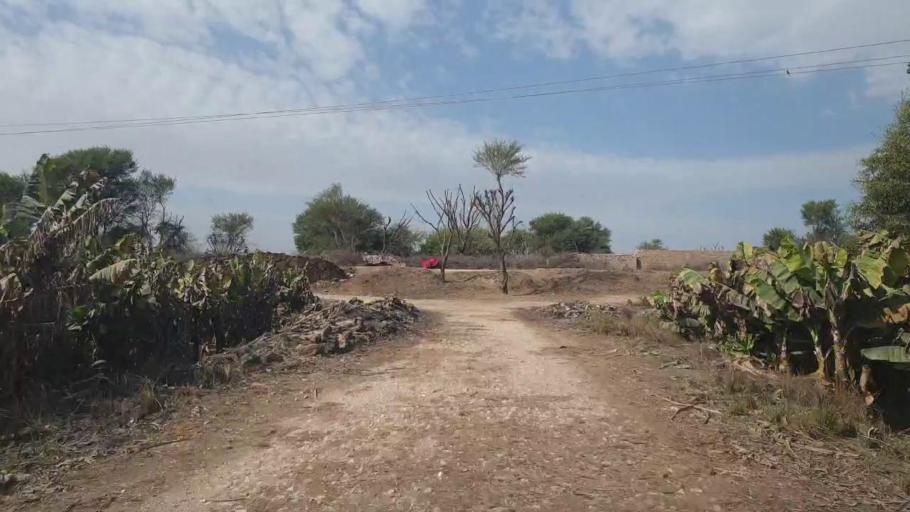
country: PK
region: Sindh
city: Sakrand
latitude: 25.9885
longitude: 68.3268
